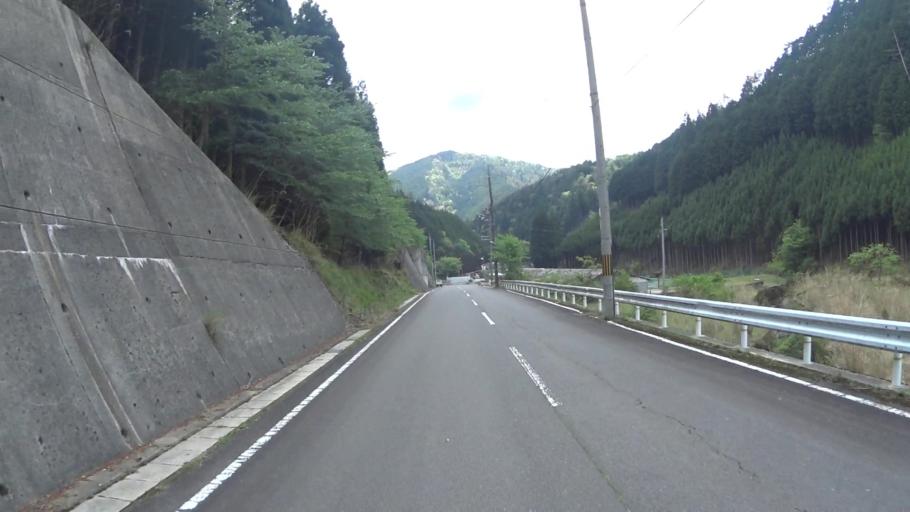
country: JP
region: Kyoto
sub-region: Kyoto-shi
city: Kamigyo-ku
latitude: 35.1187
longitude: 135.7039
